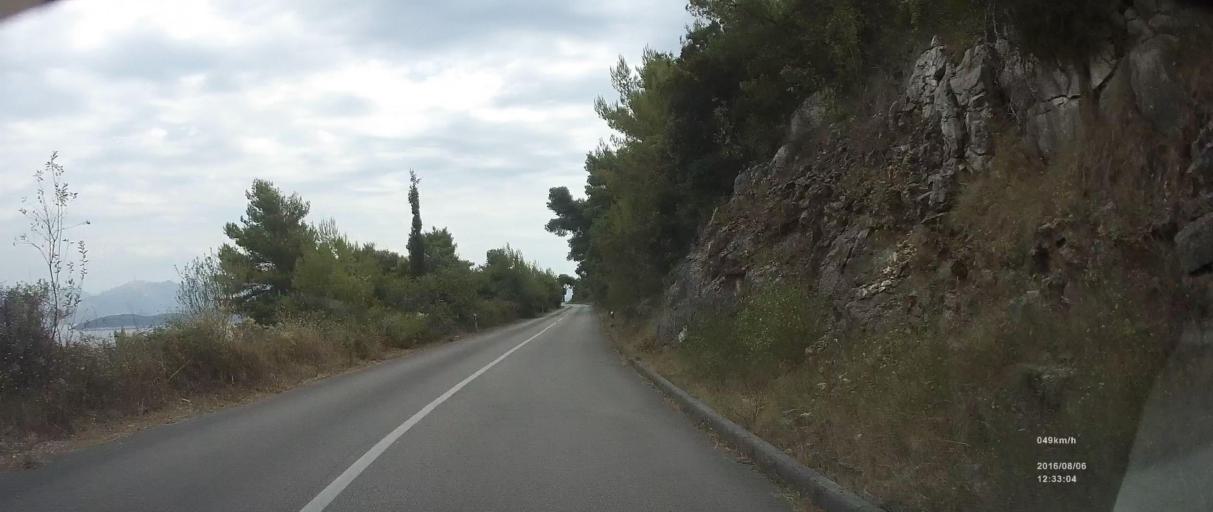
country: HR
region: Dubrovacko-Neretvanska
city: Ston
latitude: 42.7130
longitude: 17.7174
